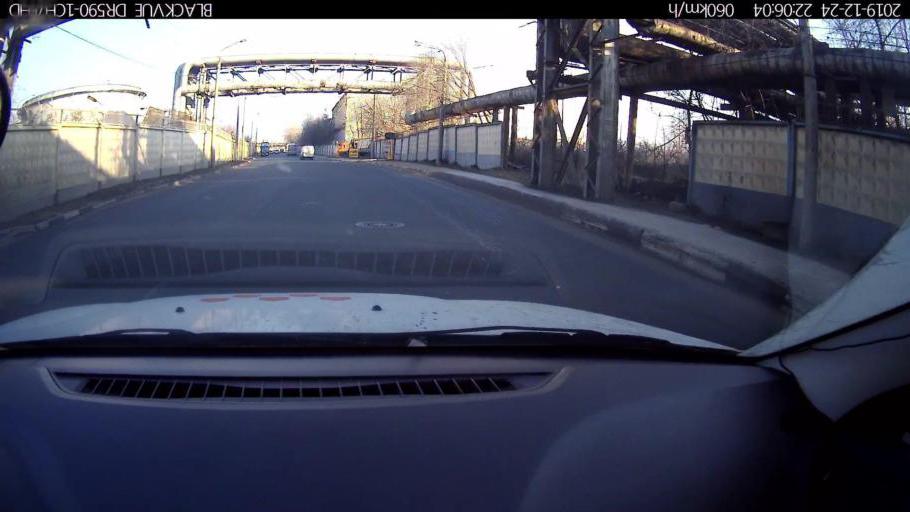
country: RU
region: Nizjnij Novgorod
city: Nizhniy Novgorod
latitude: 56.2405
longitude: 43.8955
